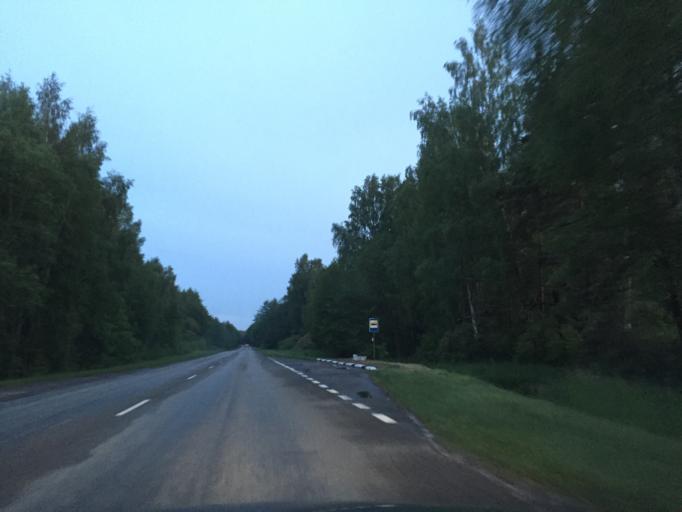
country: LT
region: Klaipedos apskritis
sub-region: Klaipeda
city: Palanga
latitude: 55.8964
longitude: 21.0663
